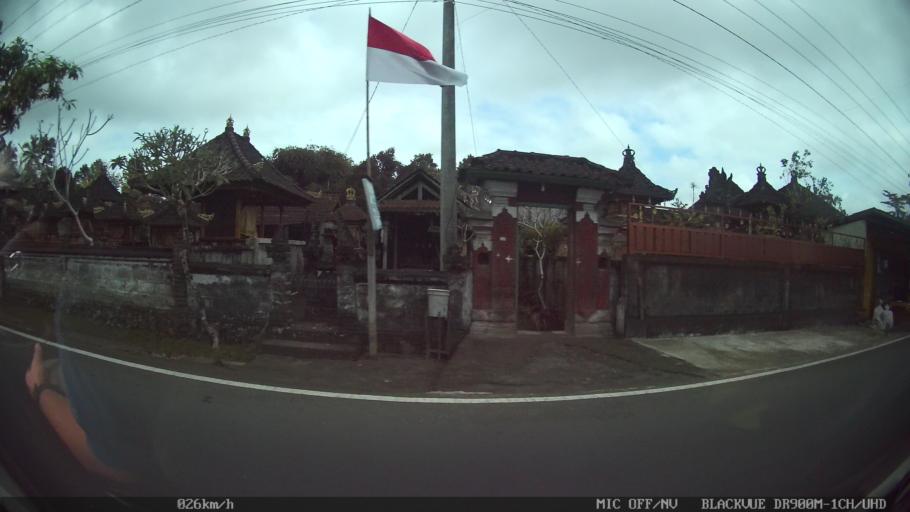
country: ID
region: Bali
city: Banjar Kubu
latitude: -8.4456
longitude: 115.4020
